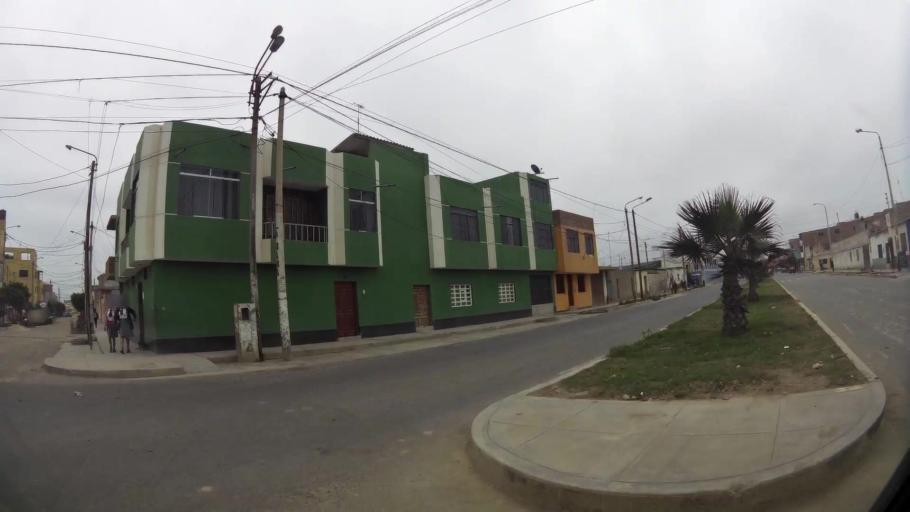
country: PE
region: La Libertad
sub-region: Provincia de Trujillo
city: Buenos Aires
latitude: -8.1458
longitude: -79.0512
